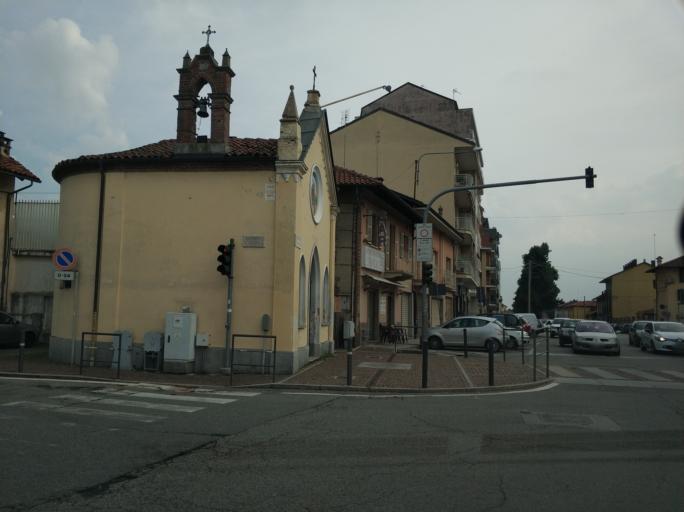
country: IT
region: Piedmont
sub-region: Provincia di Torino
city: San Carlo Canavese
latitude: 45.2380
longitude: 7.6035
